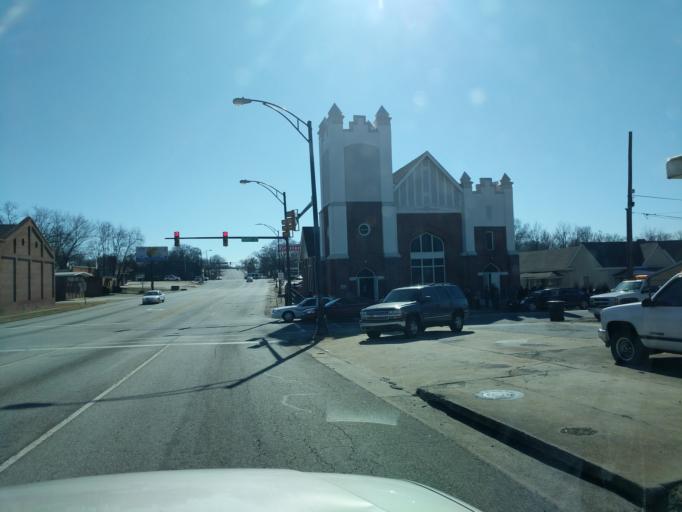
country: US
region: South Carolina
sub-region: Anderson County
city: Anderson
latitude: 34.5037
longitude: -82.6520
